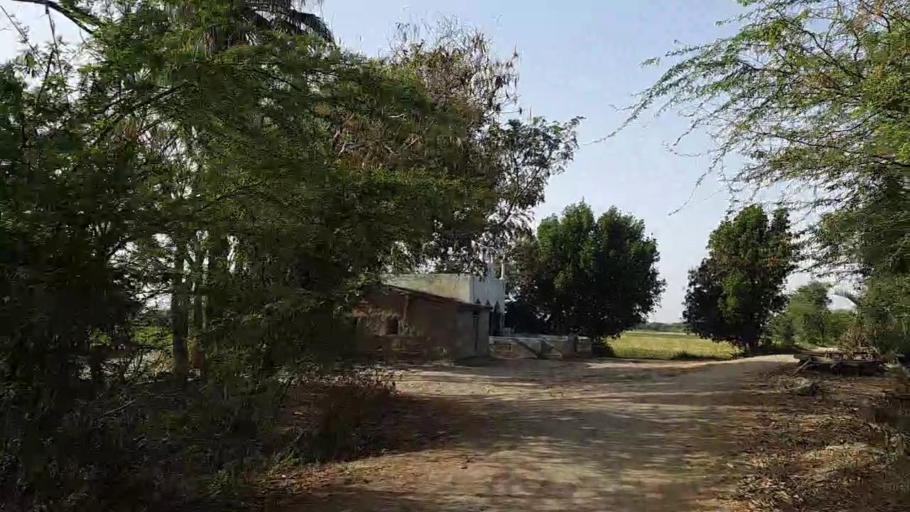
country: PK
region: Sindh
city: Jati
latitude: 24.2848
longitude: 68.1492
